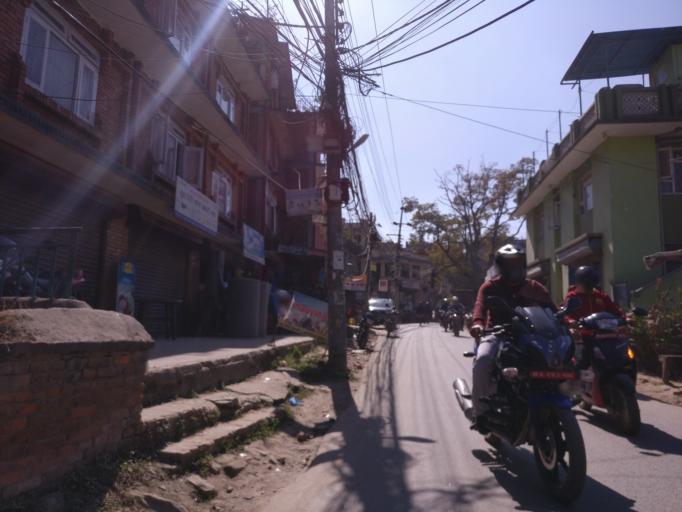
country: NP
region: Central Region
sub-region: Bagmati Zone
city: Patan
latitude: 27.6784
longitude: 85.3289
